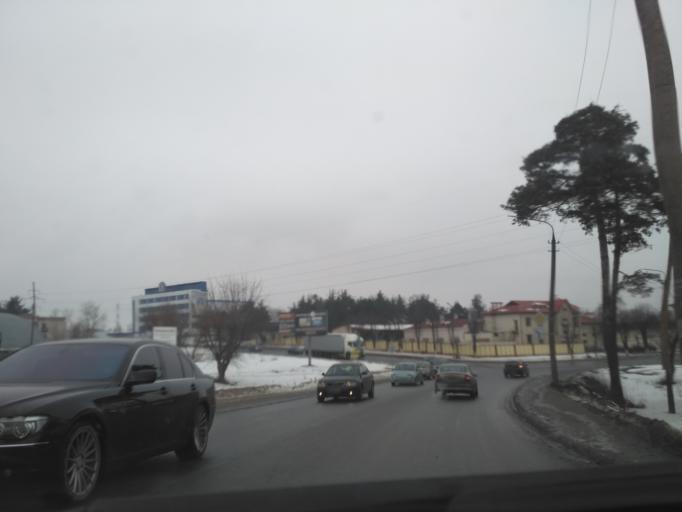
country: BY
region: Minsk
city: Horad Barysaw
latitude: 54.1971
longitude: 28.5148
